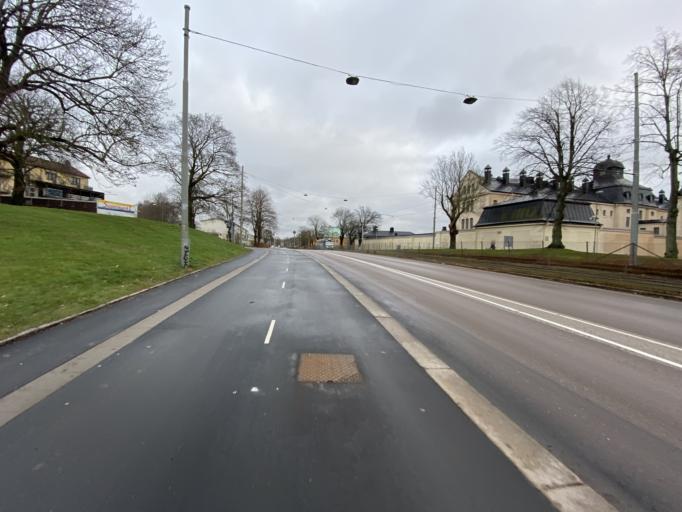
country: SE
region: Vaestra Goetaland
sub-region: Goteborg
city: Goeteborg
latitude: 57.7174
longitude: 12.0148
